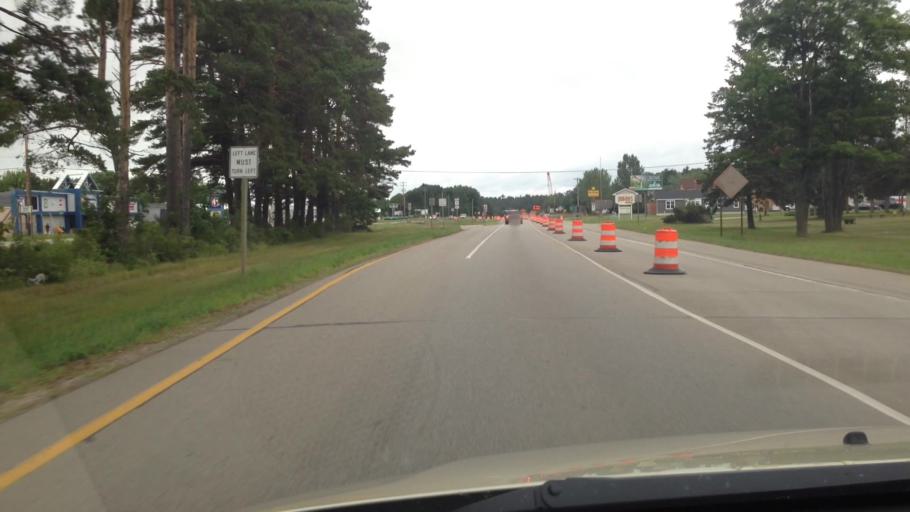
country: US
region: Michigan
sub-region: Delta County
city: Escanaba
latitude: 45.7867
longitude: -87.0820
